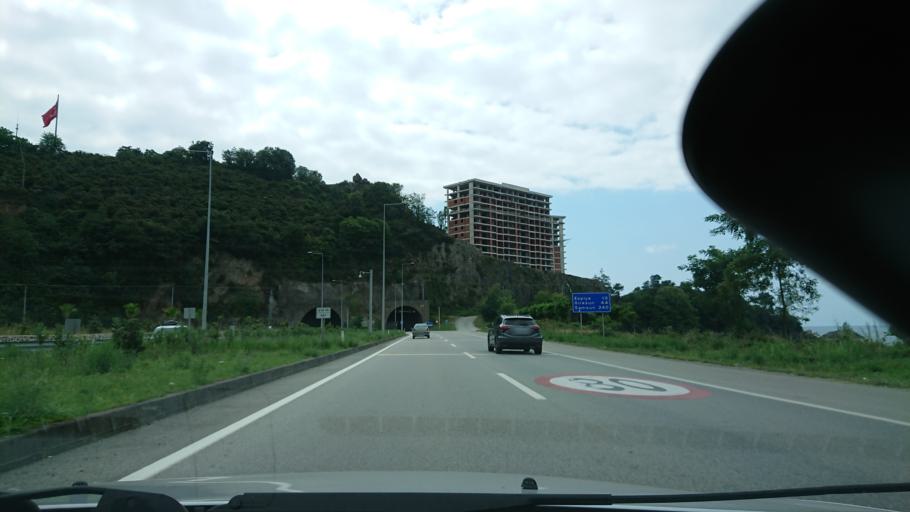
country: TR
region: Giresun
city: Tirebolu
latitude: 40.9995
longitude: 38.7990
